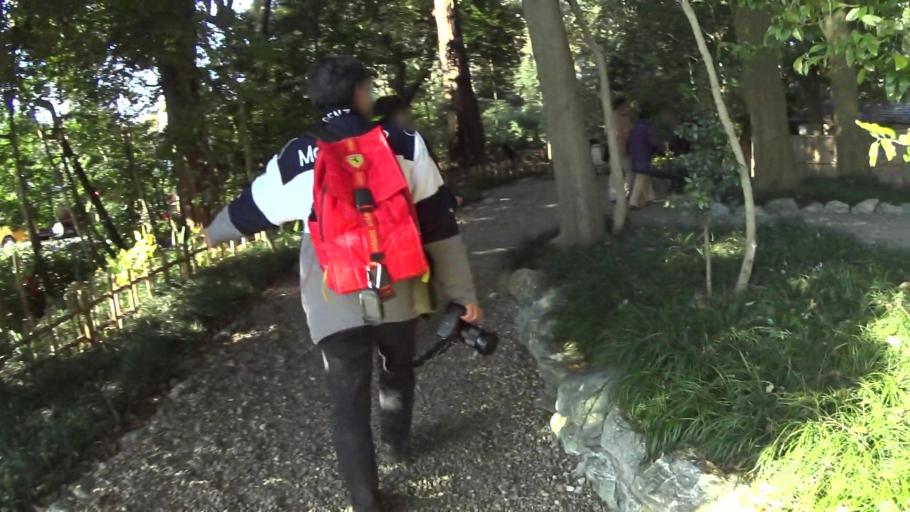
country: JP
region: Saitama
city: Saitama
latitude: 35.9163
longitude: 139.6292
